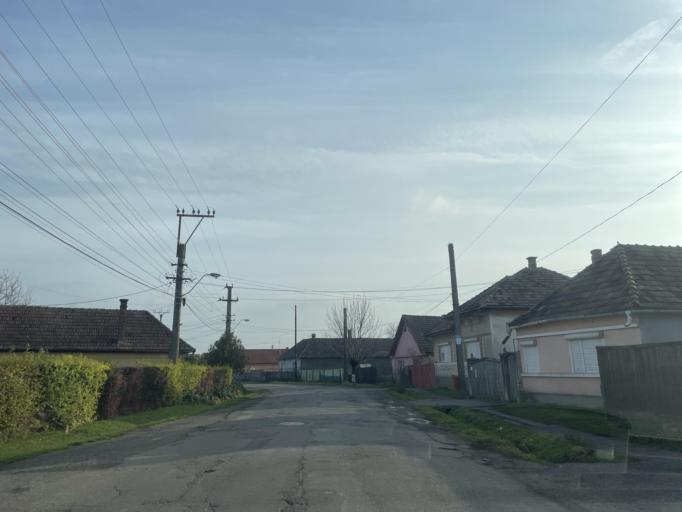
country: RO
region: Mures
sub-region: Municipiul Reghin
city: Apalina
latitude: 46.7566
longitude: 24.6930
